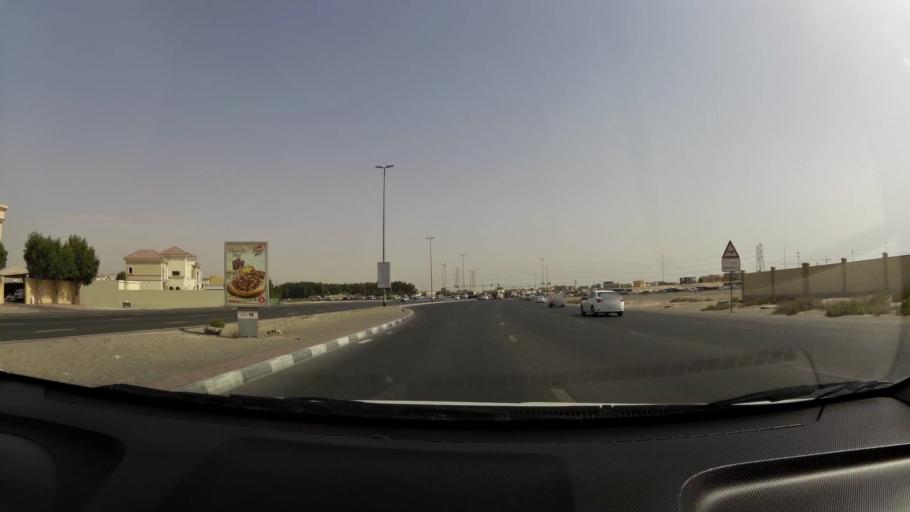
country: AE
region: Ash Shariqah
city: Sharjah
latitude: 25.2729
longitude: 55.3962
